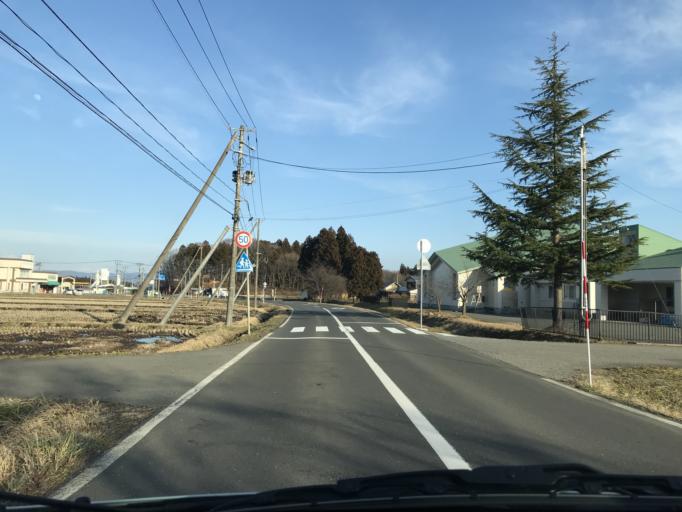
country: JP
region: Iwate
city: Kitakami
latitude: 39.2328
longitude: 141.0642
